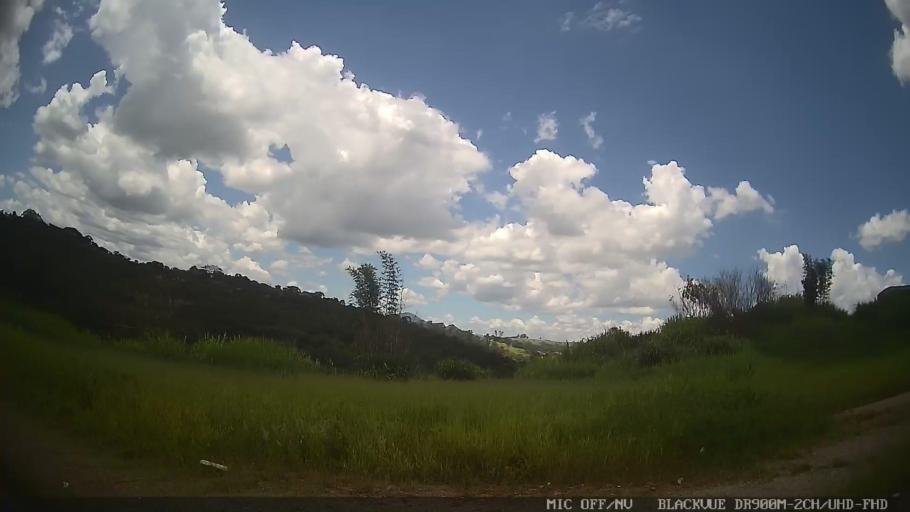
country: BR
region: Sao Paulo
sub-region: Braganca Paulista
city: Braganca Paulista
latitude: -22.9852
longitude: -46.4852
